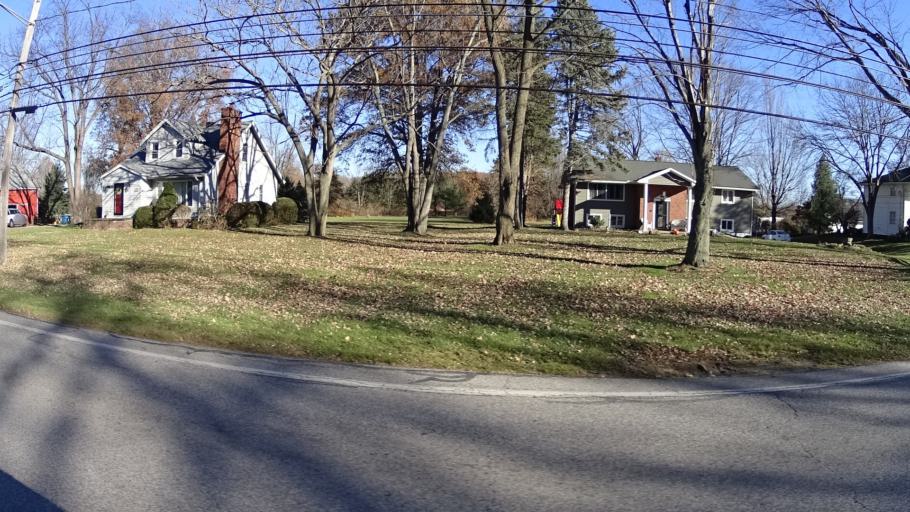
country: US
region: Ohio
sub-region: Lorain County
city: North Ridgeville
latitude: 41.4097
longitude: -82.0187
